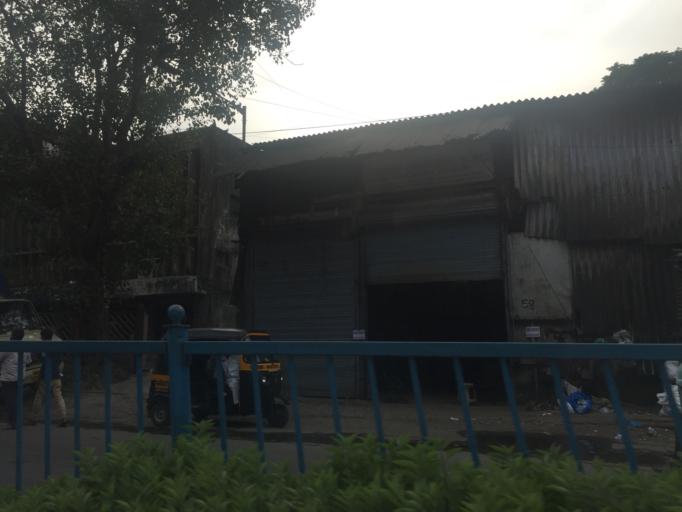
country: IN
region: Maharashtra
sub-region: Mumbai Suburban
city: Powai
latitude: 19.1198
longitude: 72.9258
